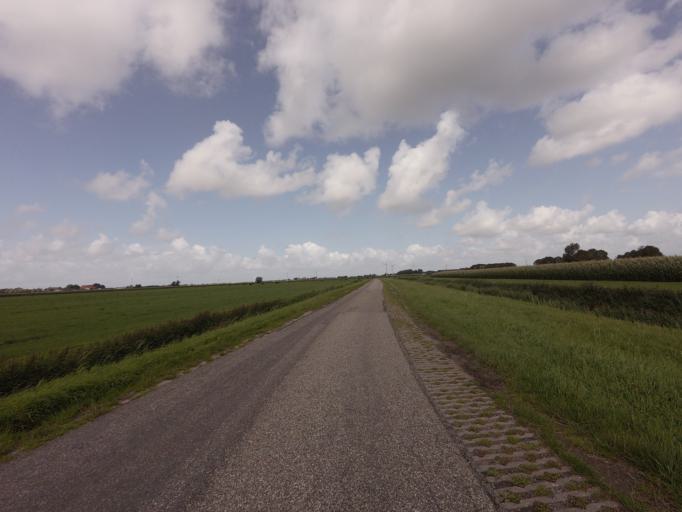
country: NL
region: Friesland
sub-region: Gemeente Franekeradeel
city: Sexbierum
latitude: 53.1682
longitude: 5.4856
